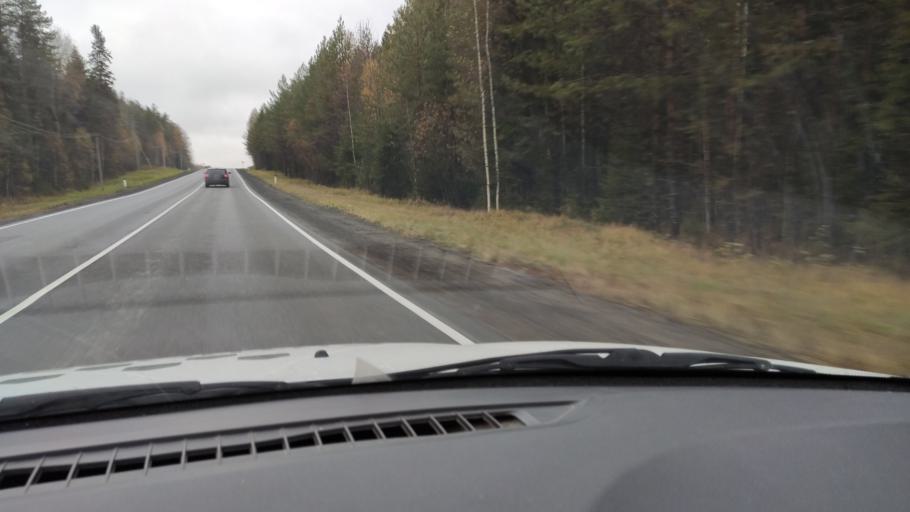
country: RU
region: Kirov
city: Belaya Kholunitsa
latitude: 58.9057
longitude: 51.0280
